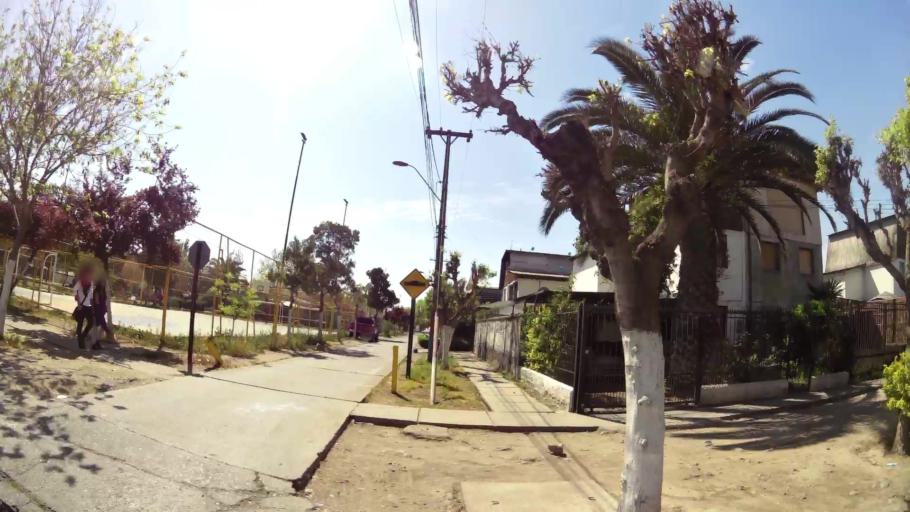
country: CL
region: Santiago Metropolitan
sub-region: Provincia de Santiago
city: La Pintana
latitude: -33.5295
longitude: -70.6421
